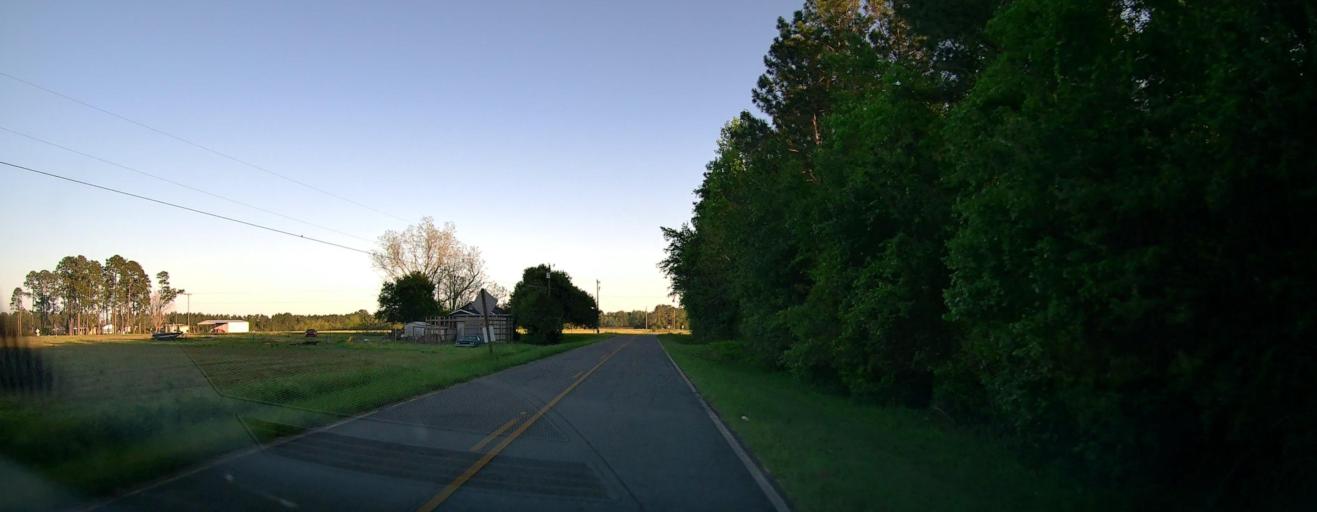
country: US
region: Georgia
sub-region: Ben Hill County
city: Fitzgerald
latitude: 31.6711
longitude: -83.2129
